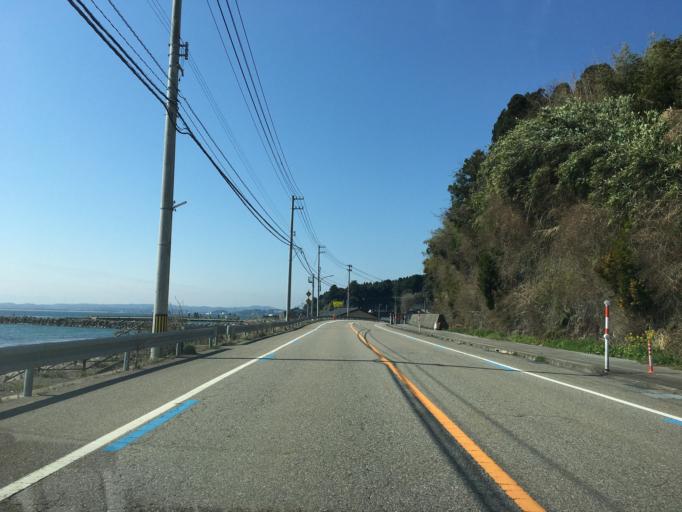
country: JP
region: Toyama
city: Himi
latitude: 36.8984
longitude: 137.0093
